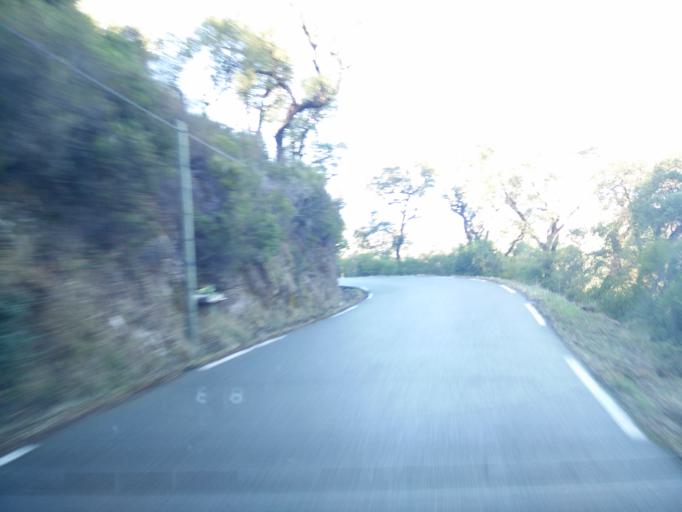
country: FR
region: Provence-Alpes-Cote d'Azur
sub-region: Departement du Var
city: La Garde-Freinet
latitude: 43.2627
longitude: 6.4708
